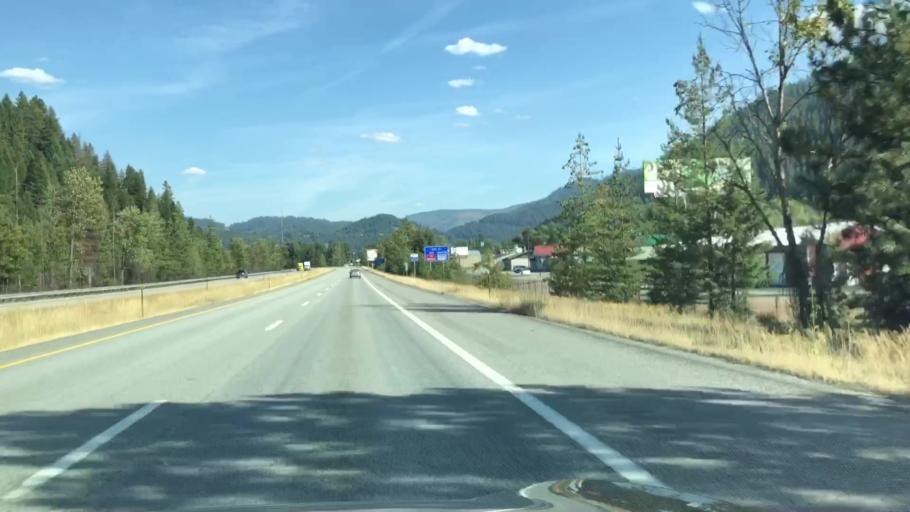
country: US
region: Idaho
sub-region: Shoshone County
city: Osburn
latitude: 47.5121
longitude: -116.0200
